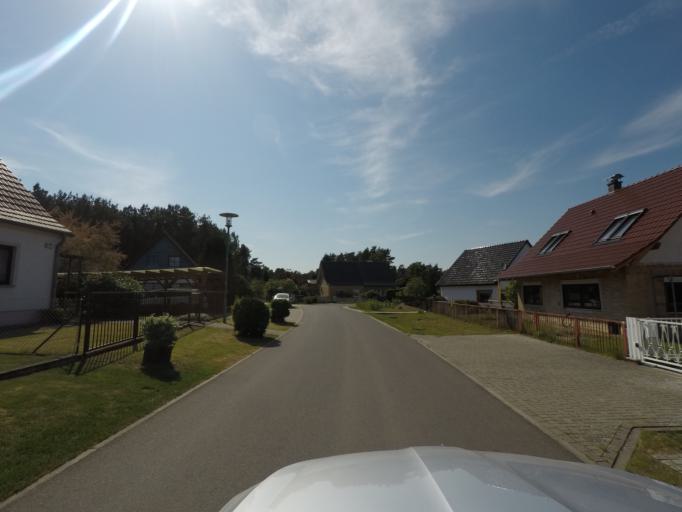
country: DE
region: Brandenburg
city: Melchow
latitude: 52.8611
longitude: 13.7178
